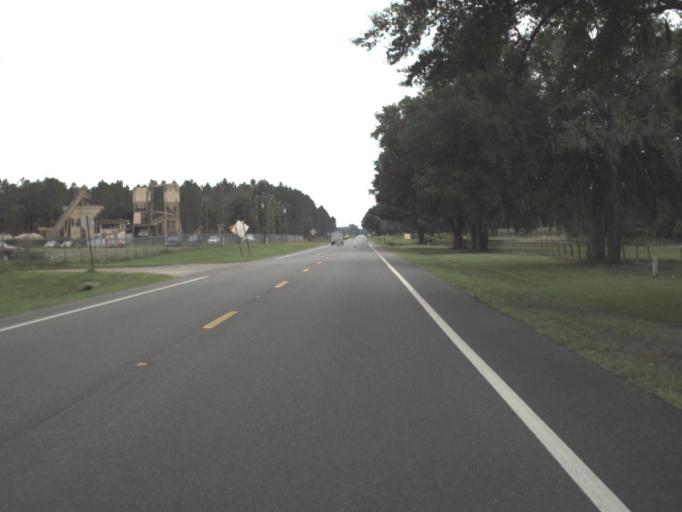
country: US
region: Florida
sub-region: Levy County
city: Williston
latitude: 29.3616
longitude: -82.4558
